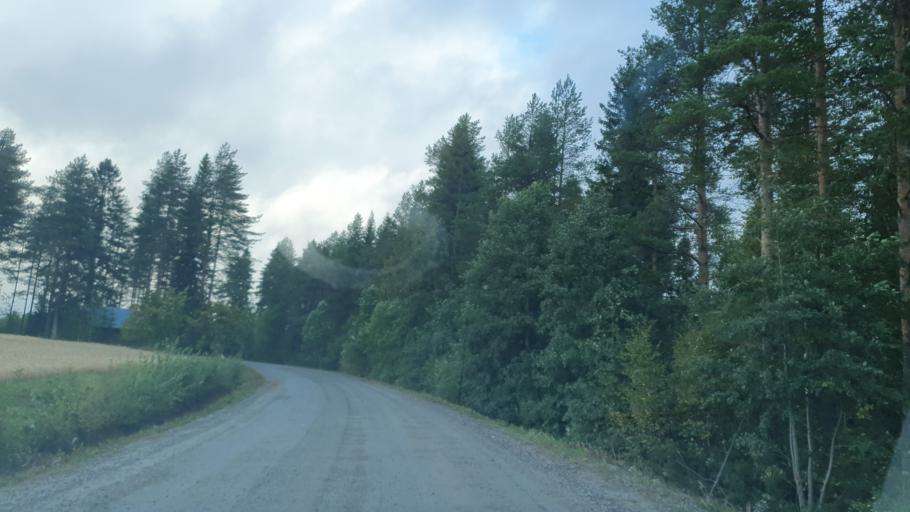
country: FI
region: Kainuu
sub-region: Kehys-Kainuu
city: Kuhmo
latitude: 64.1339
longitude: 29.5808
